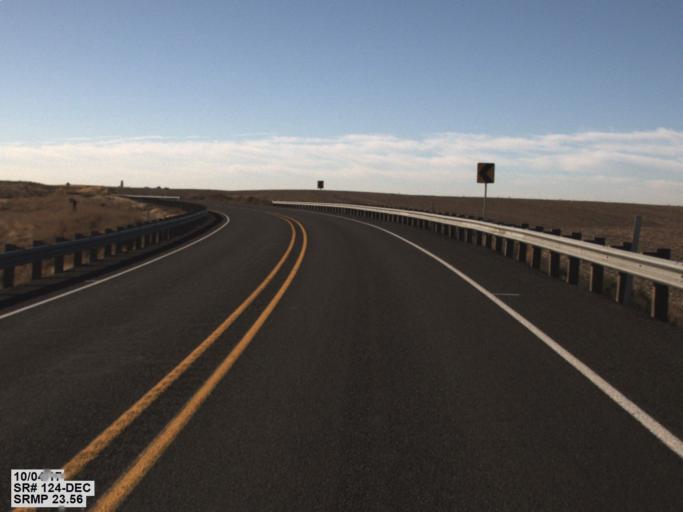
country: US
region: Washington
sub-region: Walla Walla County
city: Garrett
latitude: 46.2960
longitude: -118.5639
